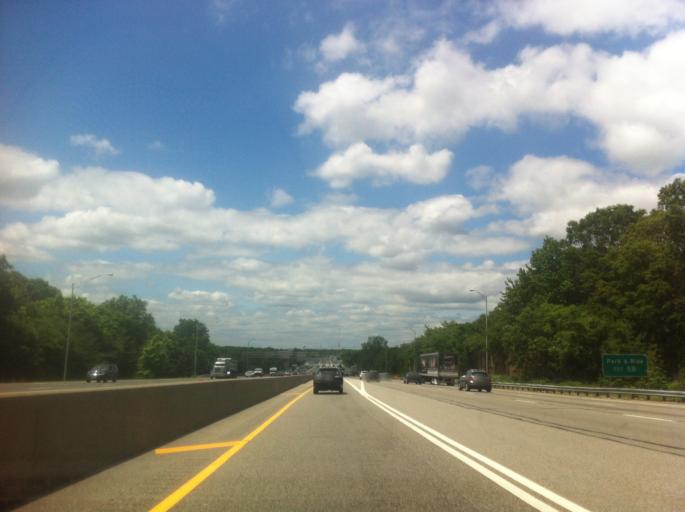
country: US
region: New York
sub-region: Suffolk County
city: Lake Ronkonkoma
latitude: 40.8114
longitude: -73.1417
